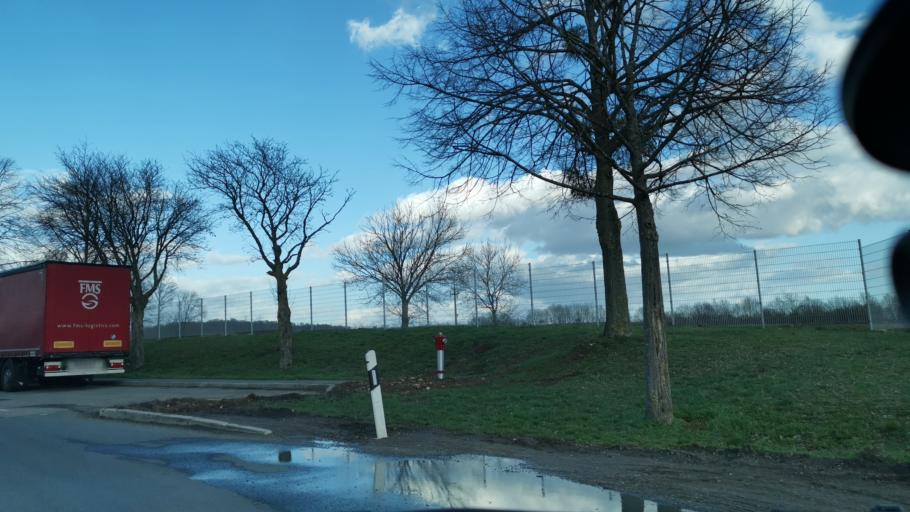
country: DE
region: Baden-Wuerttemberg
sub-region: Regierungsbezirk Stuttgart
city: Widdern
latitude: 49.3235
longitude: 9.4114
